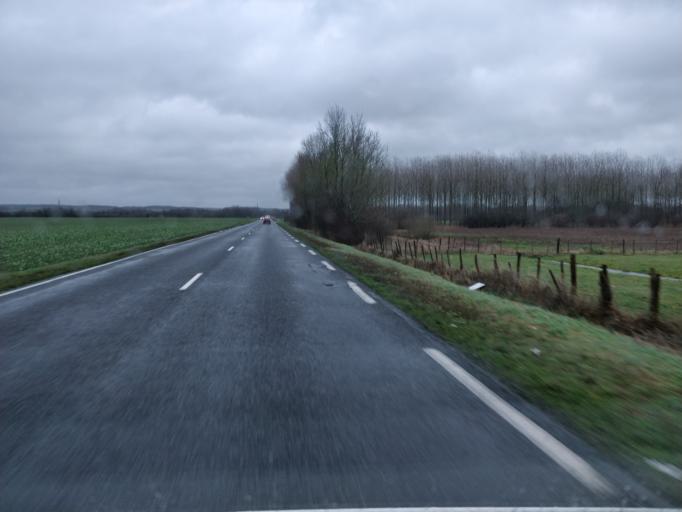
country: FR
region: Bourgogne
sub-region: Departement de l'Yonne
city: Thorigny-sur-Oreuse
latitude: 48.2290
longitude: 3.5166
